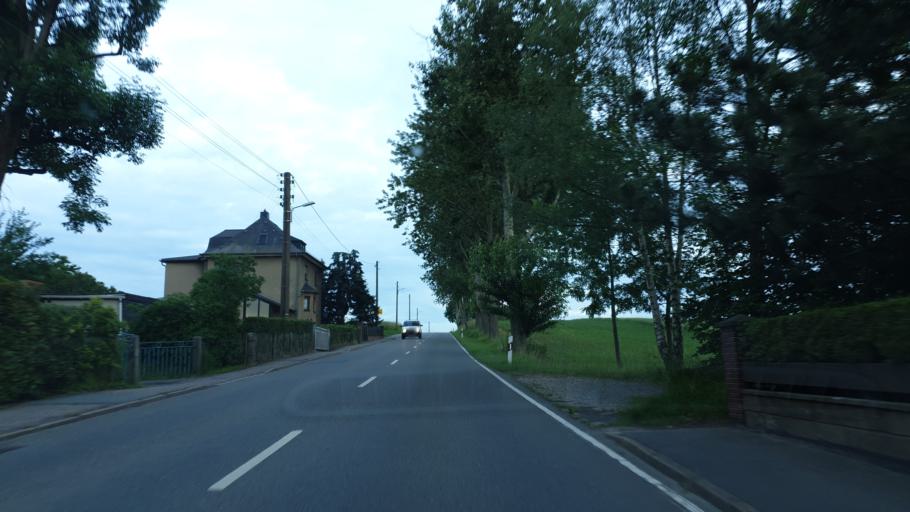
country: DE
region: Saxony
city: Hohenstein-Ernstthal
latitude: 50.7959
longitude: 12.7169
